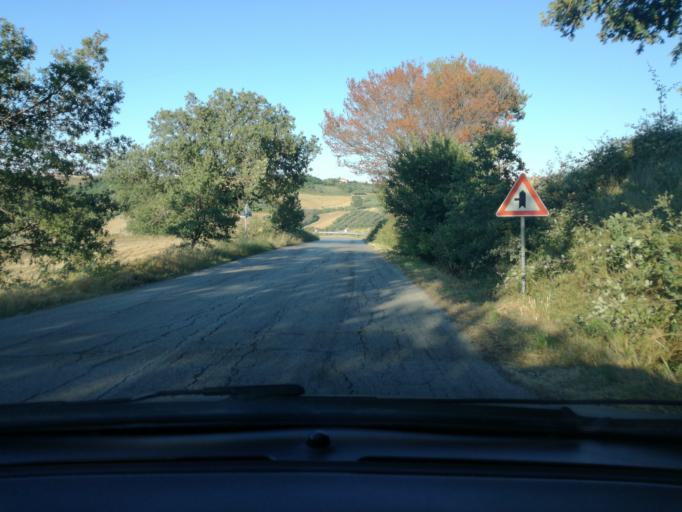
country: IT
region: Molise
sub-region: Provincia di Campobasso
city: Guglionesi
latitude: 41.9352
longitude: 14.9315
